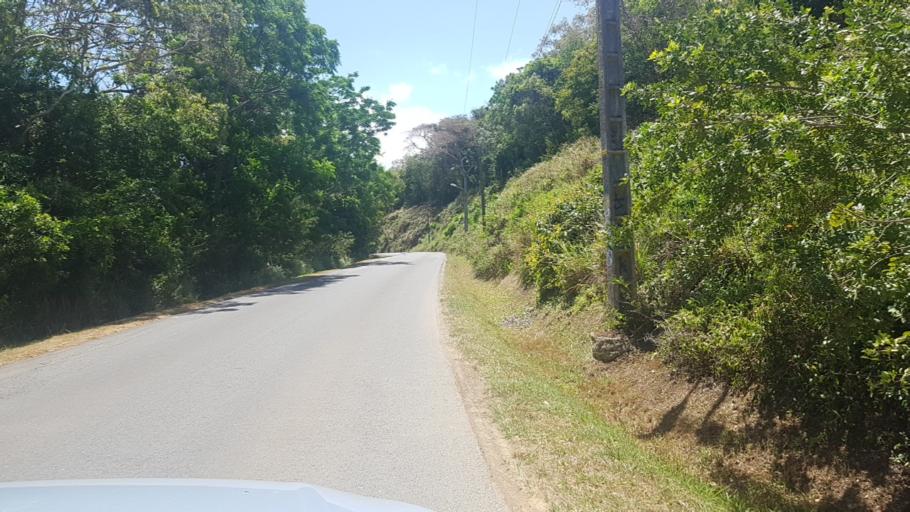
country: NC
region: South Province
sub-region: Dumbea
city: Dumbea
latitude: -22.1386
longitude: 166.4383
